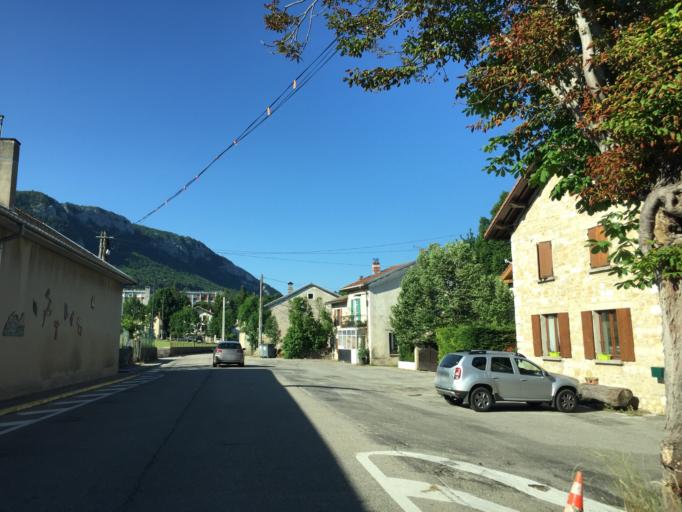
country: FR
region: Rhone-Alpes
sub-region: Departement de la Drome
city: Saint-Laurent-en-Royans
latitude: 44.9665
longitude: 5.4150
